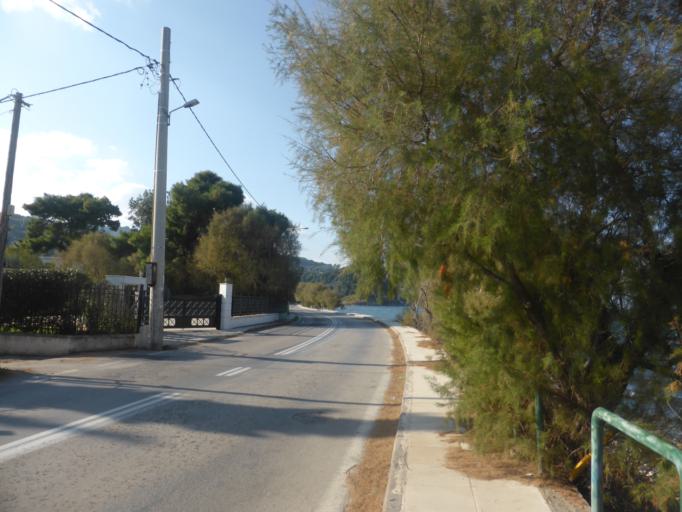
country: GR
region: Attica
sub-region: Nomarchia Anatolikis Attikis
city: Kalamos
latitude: 38.3077
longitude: 23.8612
